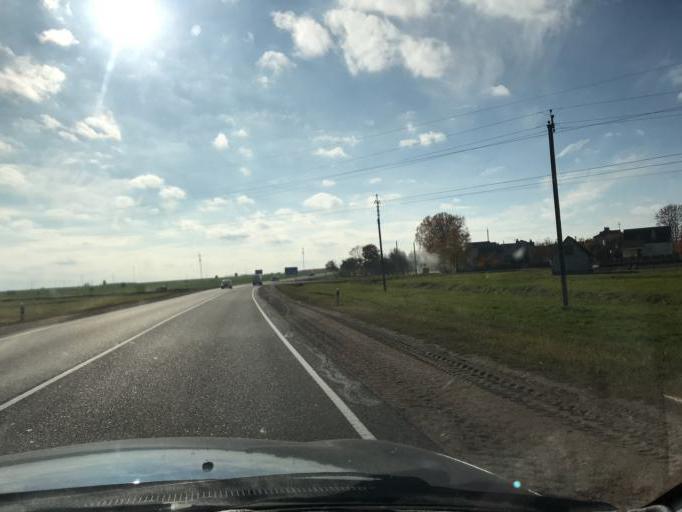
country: BY
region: Grodnenskaya
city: Voranava
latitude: 54.1475
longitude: 25.3268
